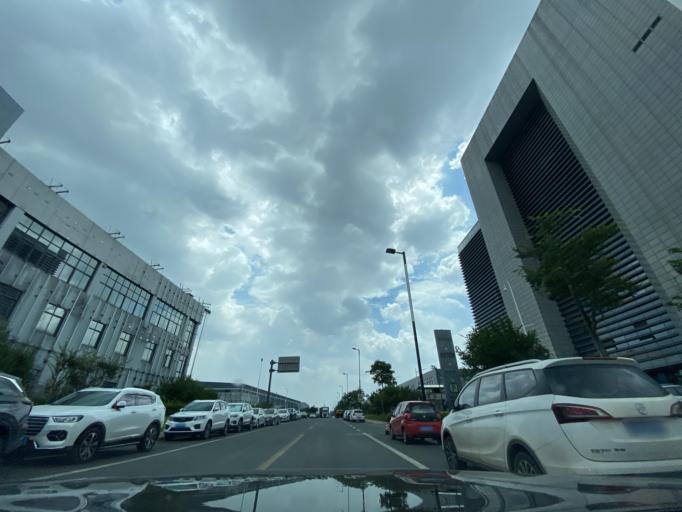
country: CN
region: Sichuan
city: Longquan
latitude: 30.5333
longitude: 104.1966
